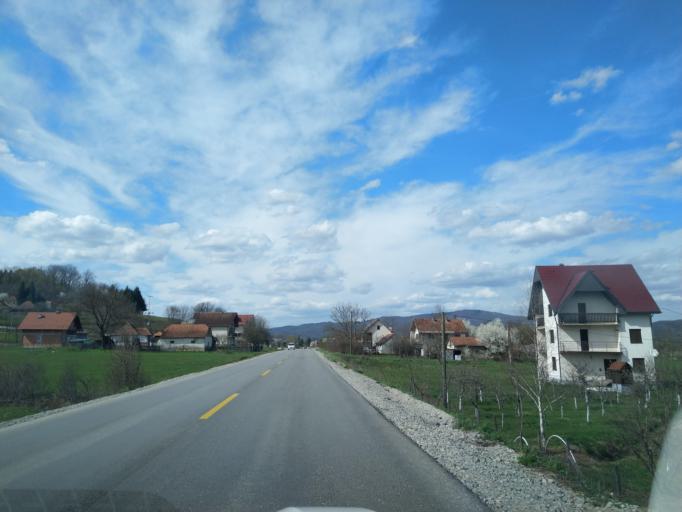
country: RS
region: Central Serbia
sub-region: Zlatiborski Okrug
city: Arilje
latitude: 43.8122
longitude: 20.0896
